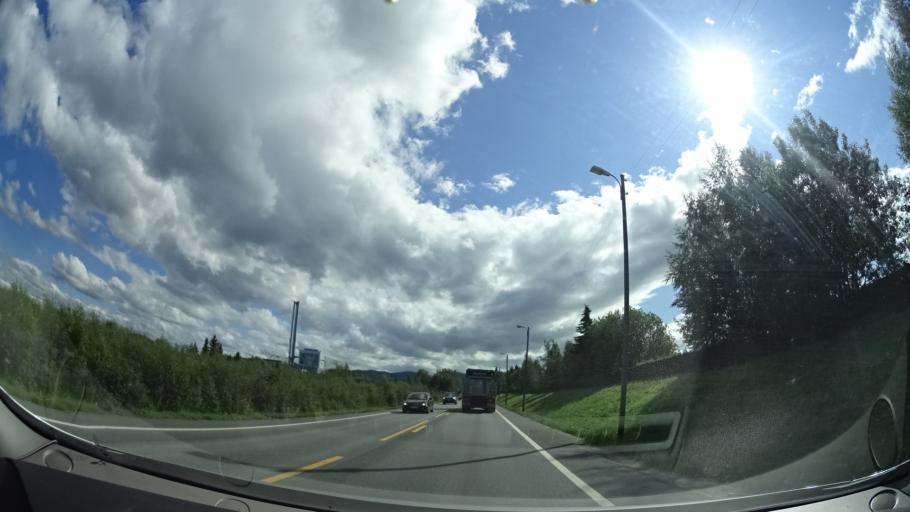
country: NO
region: Sor-Trondelag
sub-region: Trondheim
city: Trondheim
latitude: 63.3519
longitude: 10.3700
